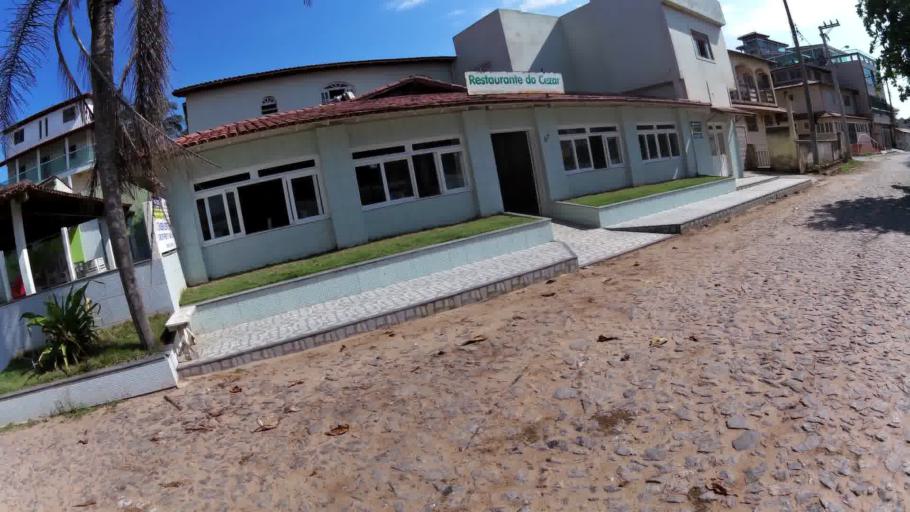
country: BR
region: Espirito Santo
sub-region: Guarapari
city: Guarapari
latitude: -20.7286
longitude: -40.5222
